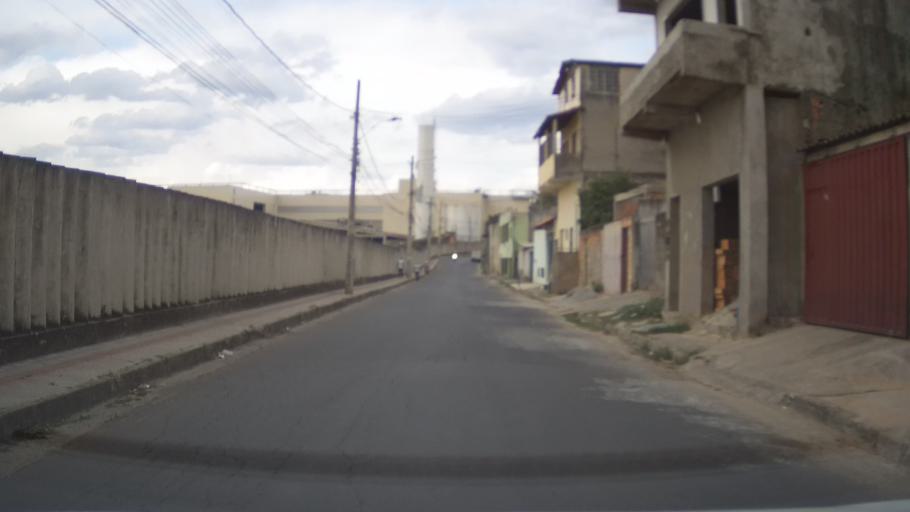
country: BR
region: Minas Gerais
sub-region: Belo Horizonte
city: Belo Horizonte
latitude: -19.8773
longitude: -43.9250
